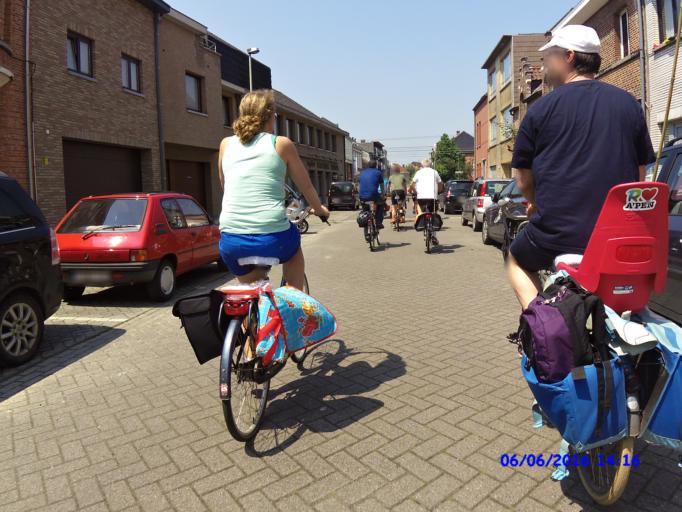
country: BE
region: Flanders
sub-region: Provincie Oost-Vlaanderen
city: Beveren
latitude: 51.2076
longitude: 4.2594
